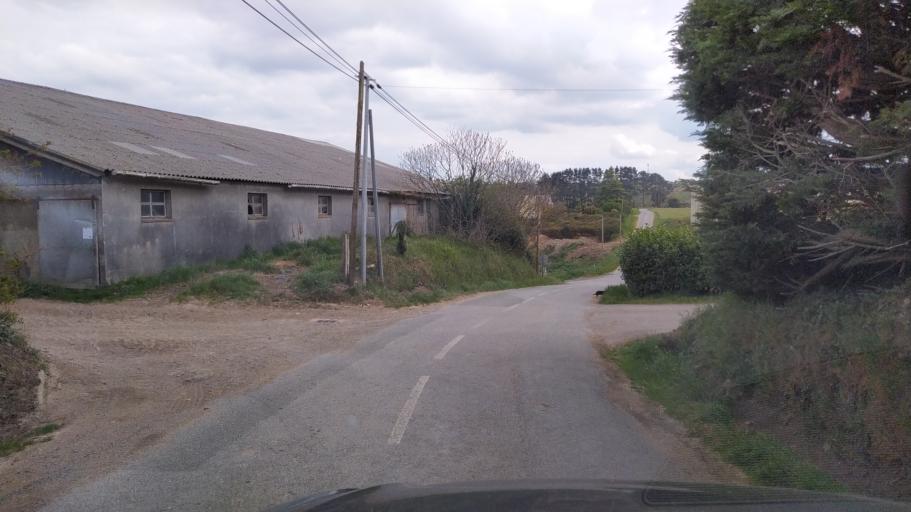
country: FR
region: Brittany
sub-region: Departement du Finistere
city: Bodilis
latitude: 48.5015
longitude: -4.1037
